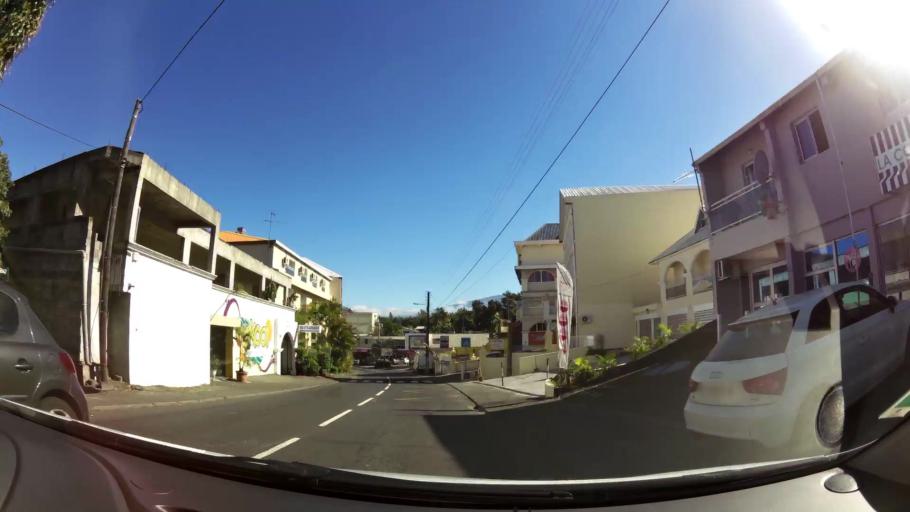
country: RE
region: Reunion
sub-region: Reunion
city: Le Tampon
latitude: -21.2833
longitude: 55.5222
